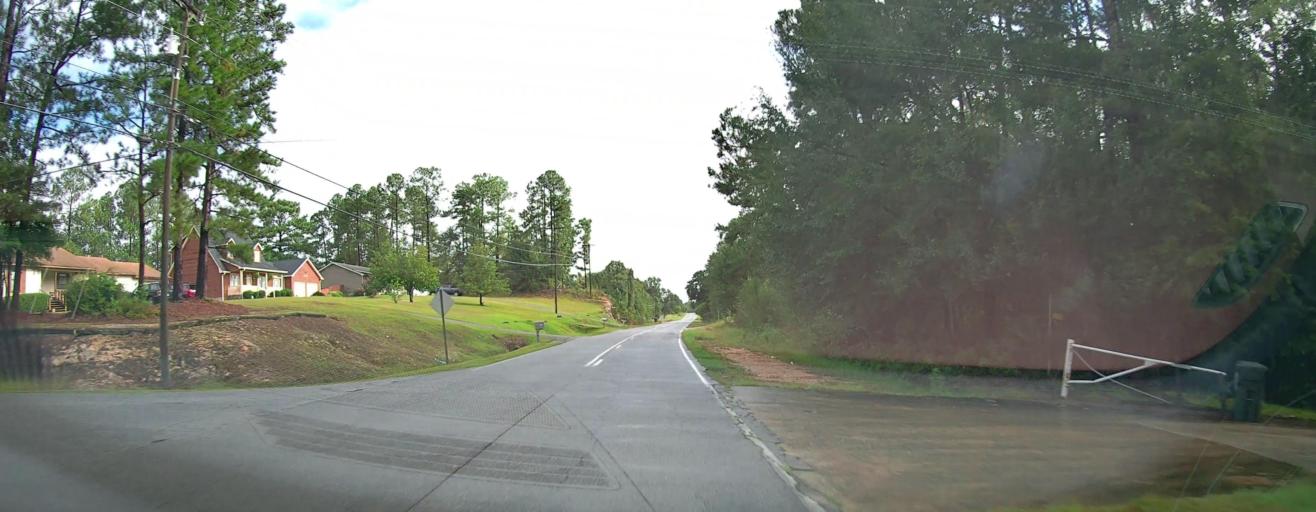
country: US
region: Georgia
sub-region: Bibb County
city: West Point
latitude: 32.7682
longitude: -83.7586
